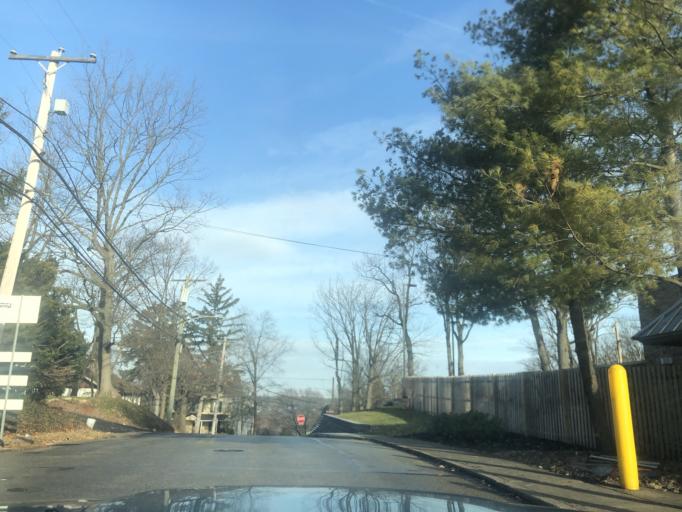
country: US
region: Pennsylvania
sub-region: Montgomery County
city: Glenside
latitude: 40.1174
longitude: -75.1379
